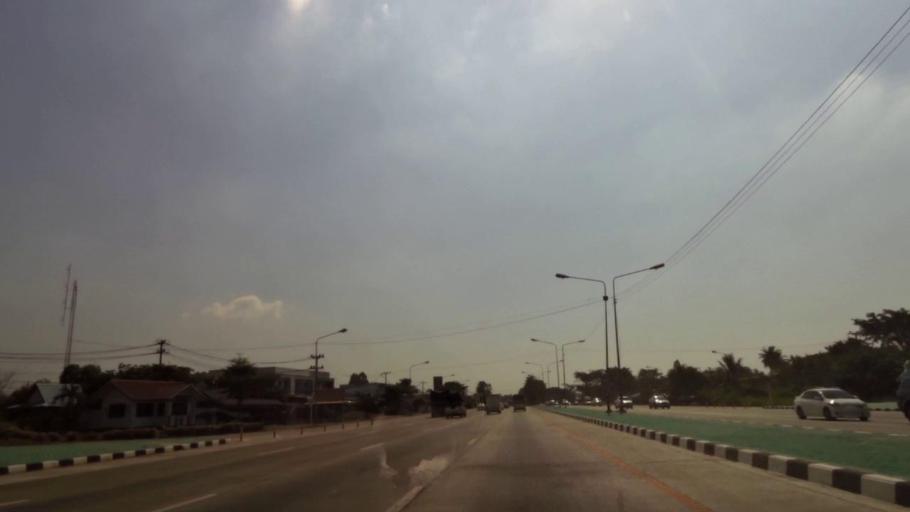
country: TH
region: Phichit
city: Bueng Na Rang
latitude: 16.1235
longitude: 100.1256
